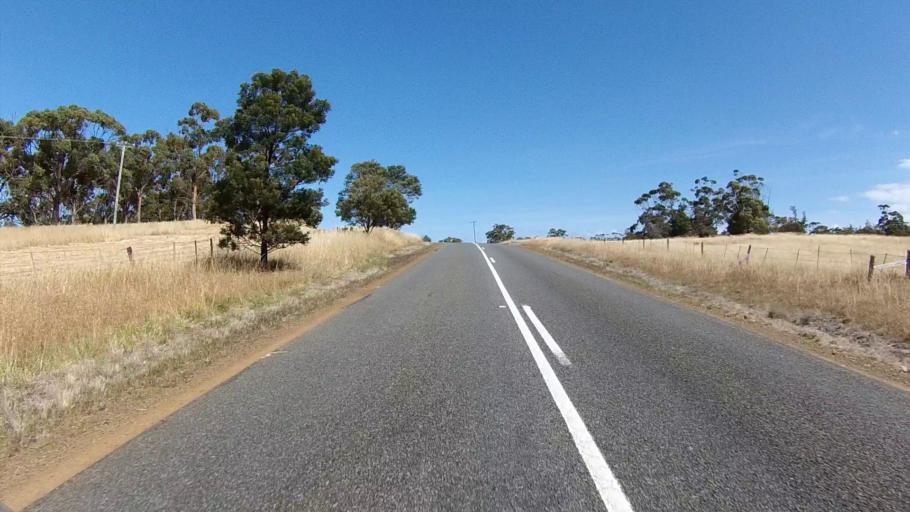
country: AU
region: Tasmania
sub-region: Sorell
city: Sorell
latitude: -42.2817
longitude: 147.9992
